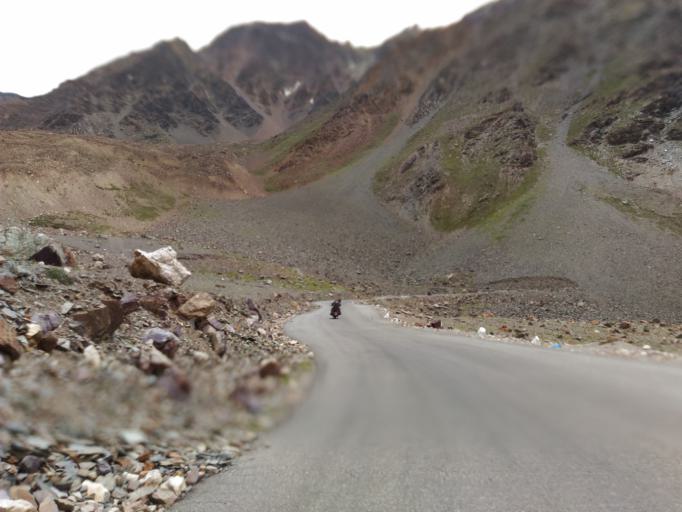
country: IN
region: Himachal Pradesh
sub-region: Lahul and Spiti
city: Kyelang
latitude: 32.7923
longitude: 77.3268
